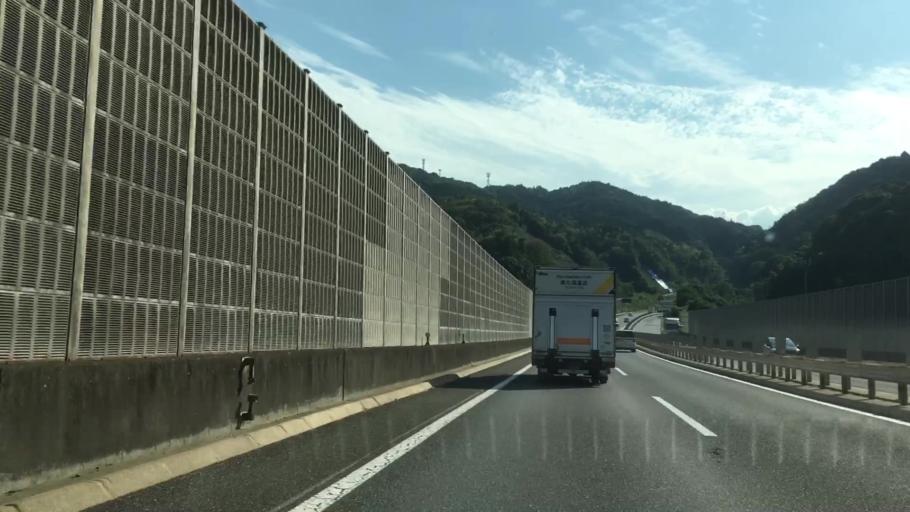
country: JP
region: Yamaguchi
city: Otake
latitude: 34.2365
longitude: 132.2139
